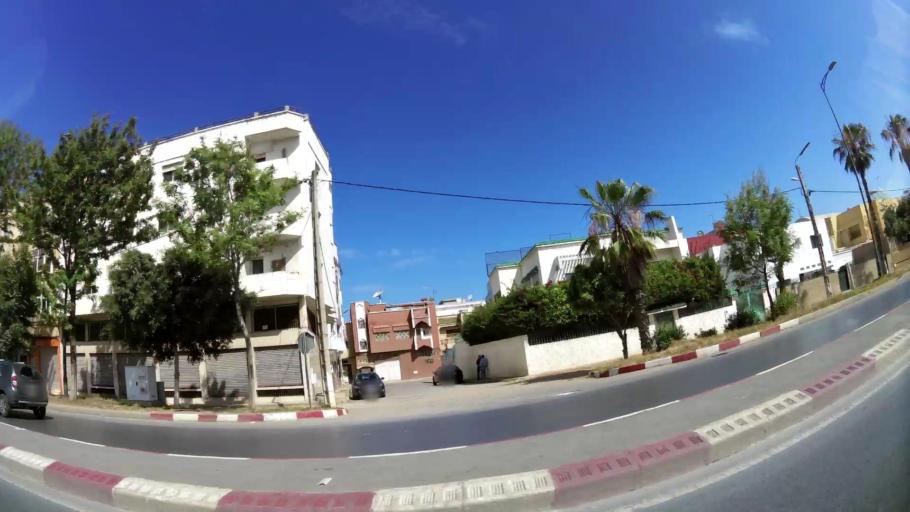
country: MA
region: Rabat-Sale-Zemmour-Zaer
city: Sale
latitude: 34.0649
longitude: -6.7963
